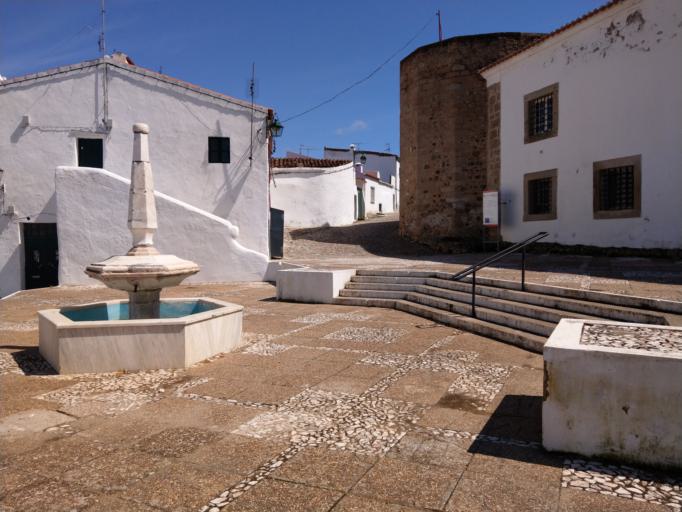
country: PT
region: Portalegre
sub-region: Campo Maior
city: Campo Maior
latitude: 39.0117
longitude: -7.0718
